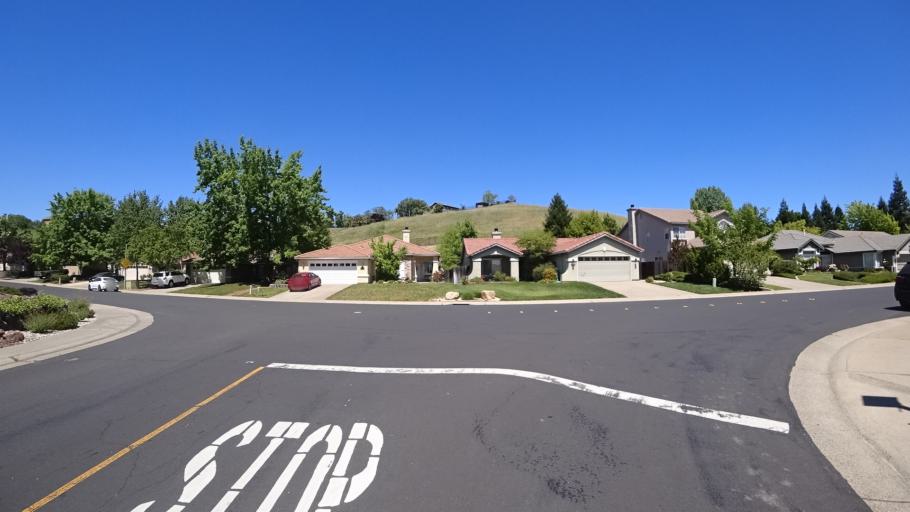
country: US
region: California
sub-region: Placer County
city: Rocklin
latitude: 38.8225
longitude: -121.2661
